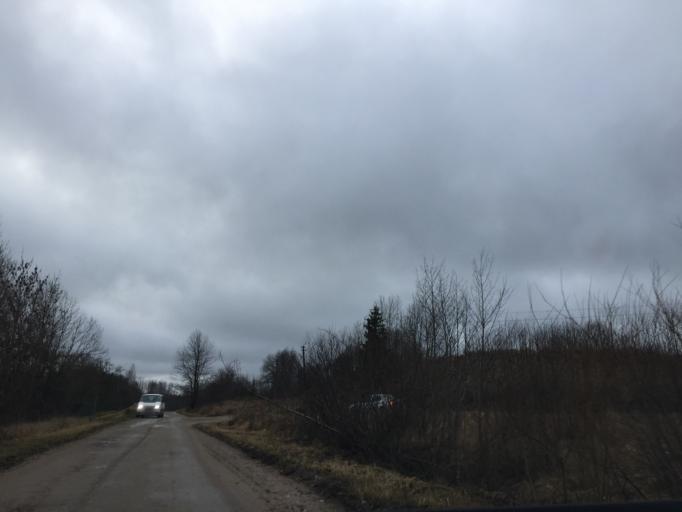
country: LV
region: Broceni
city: Broceni
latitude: 56.6675
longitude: 22.5535
